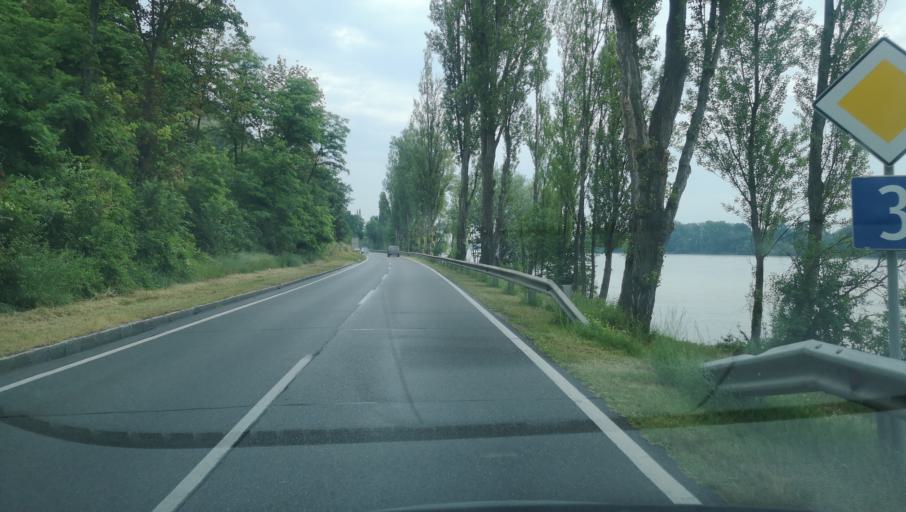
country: AT
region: Lower Austria
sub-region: Politischer Bezirk Krems
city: Senftenberg
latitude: 48.3931
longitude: 15.5587
